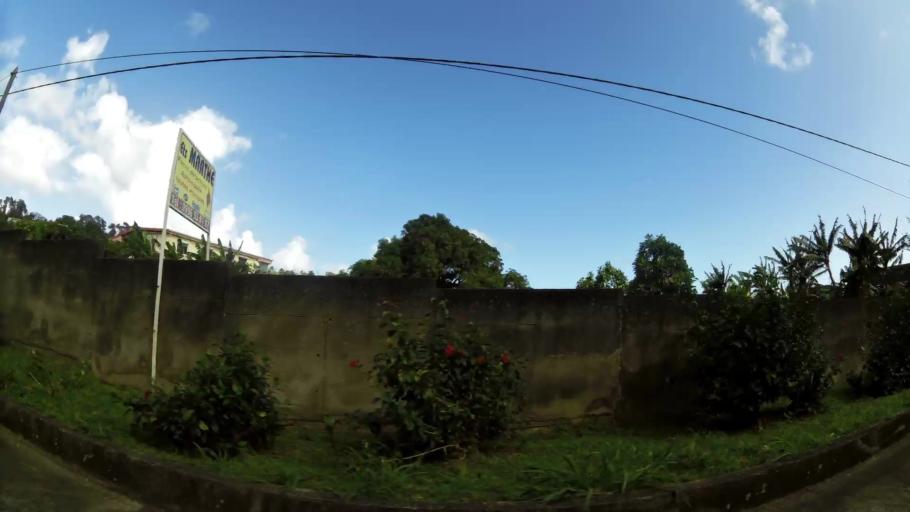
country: MQ
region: Martinique
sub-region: Martinique
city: Le Lorrain
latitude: 14.8332
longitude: -61.0663
